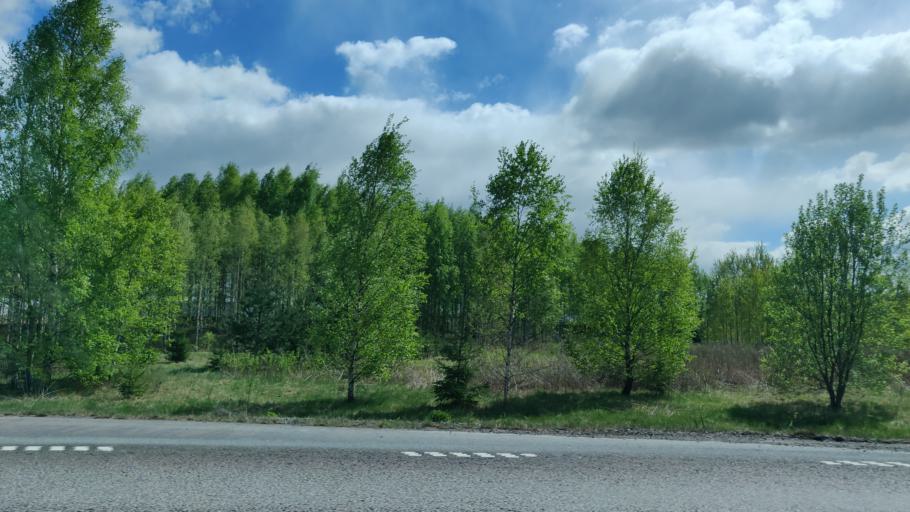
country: SE
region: Vaermland
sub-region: Karlstads Kommun
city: Molkom
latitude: 59.5485
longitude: 13.6531
